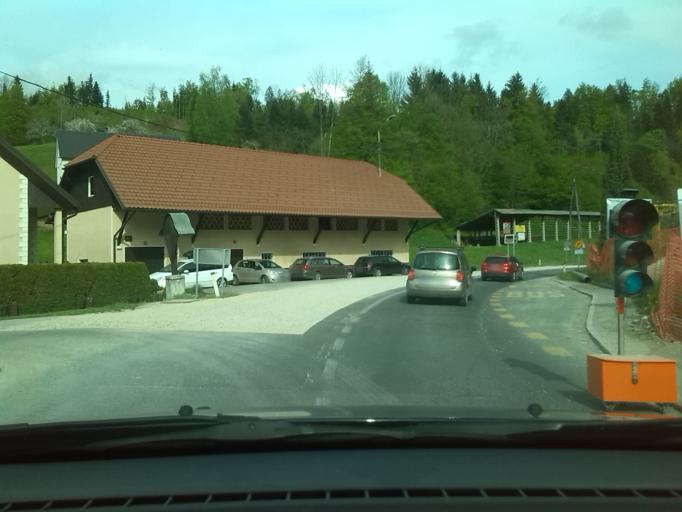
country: SI
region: Kamnik
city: Mekinje
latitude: 46.2306
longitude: 14.6377
